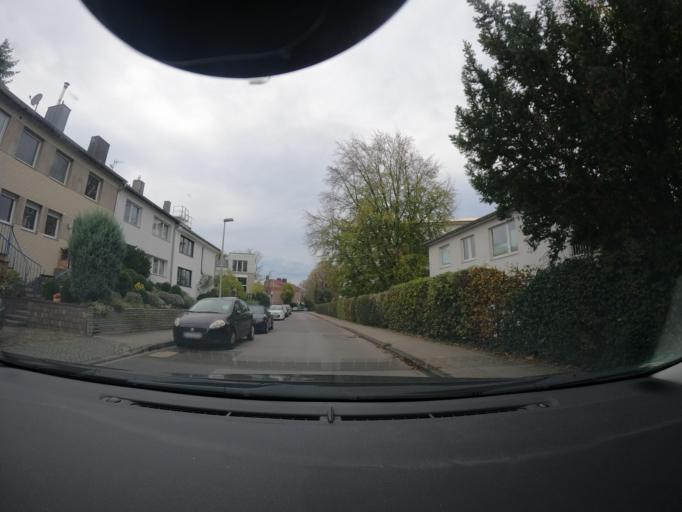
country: DE
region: North Rhine-Westphalia
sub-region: Regierungsbezirk Koln
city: Aachen
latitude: 50.7563
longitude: 6.0843
